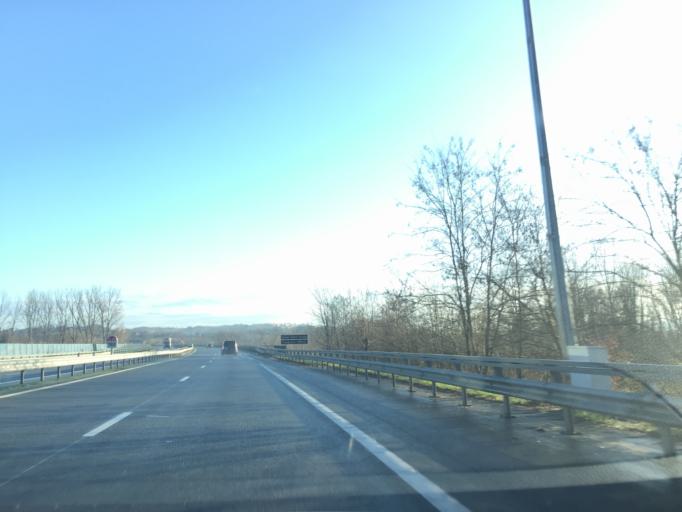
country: FR
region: Limousin
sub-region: Departement de la Correze
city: Saint-Pantaleon-de-Larche
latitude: 45.1642
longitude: 1.4539
